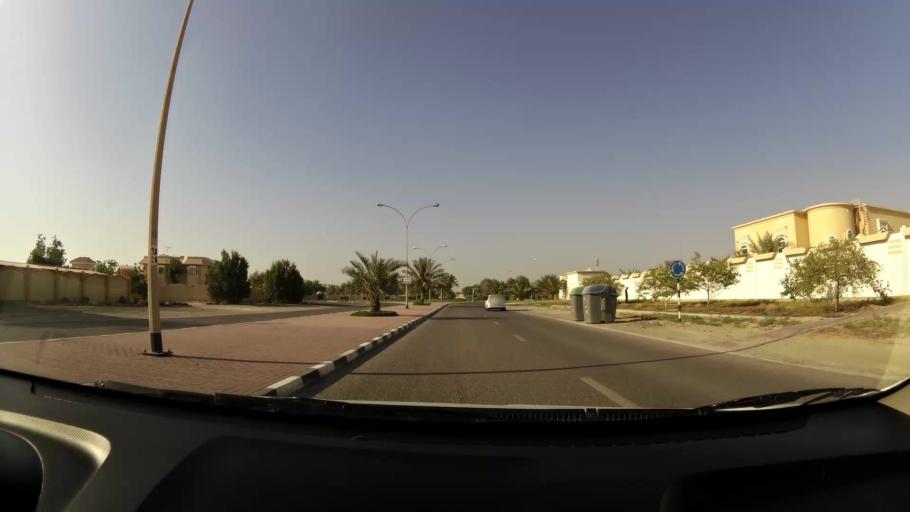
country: AE
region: Ajman
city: Ajman
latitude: 25.4073
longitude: 55.4649
